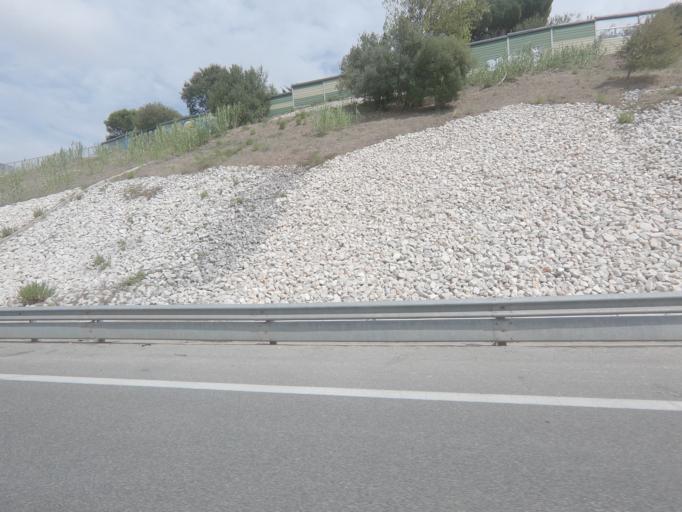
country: PT
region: Leiria
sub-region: Leiria
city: Leiria
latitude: 39.7469
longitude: -8.8188
